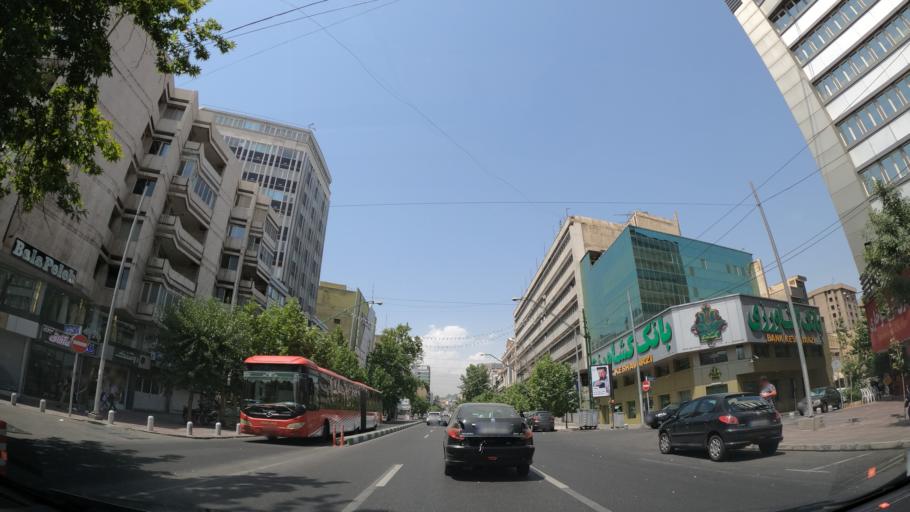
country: IR
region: Tehran
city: Tehran
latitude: 35.7170
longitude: 51.4133
